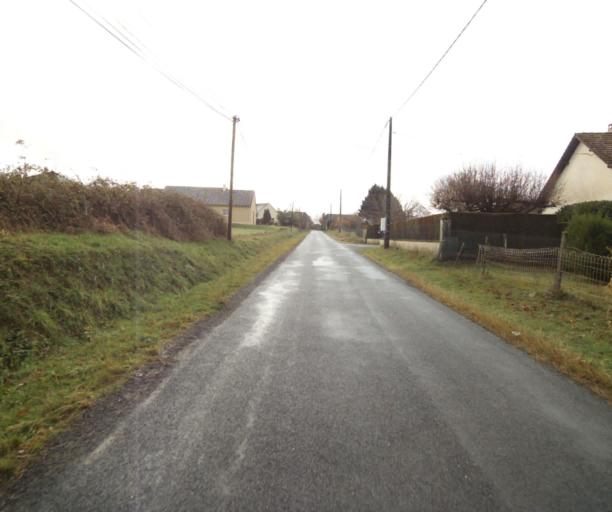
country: FR
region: Limousin
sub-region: Departement de la Correze
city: Cornil
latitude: 45.2216
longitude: 1.6441
